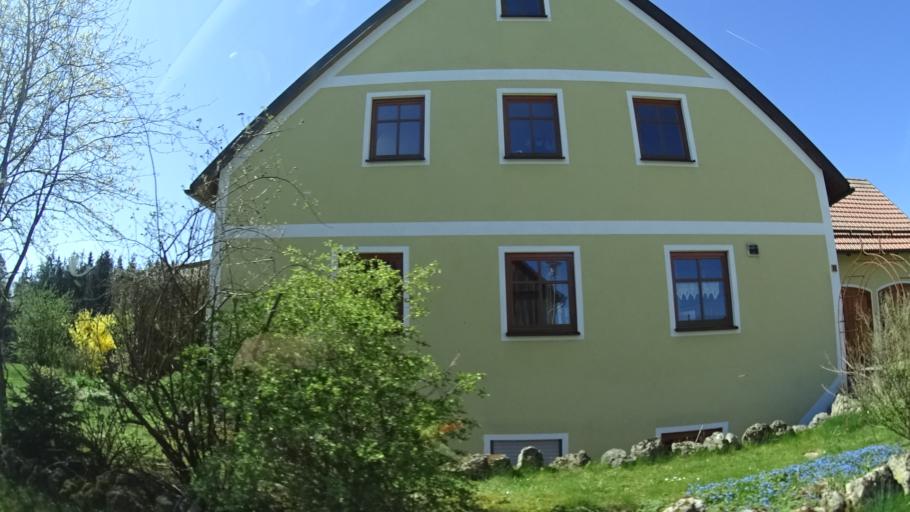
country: DE
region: Bavaria
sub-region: Upper Palatinate
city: Kastl
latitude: 49.3983
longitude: 11.6724
